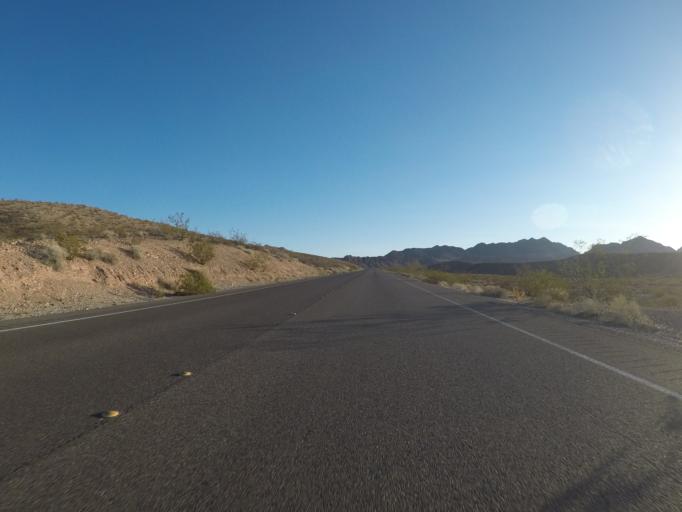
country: US
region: Nevada
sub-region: Clark County
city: Moapa Valley
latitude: 36.2701
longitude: -114.4830
